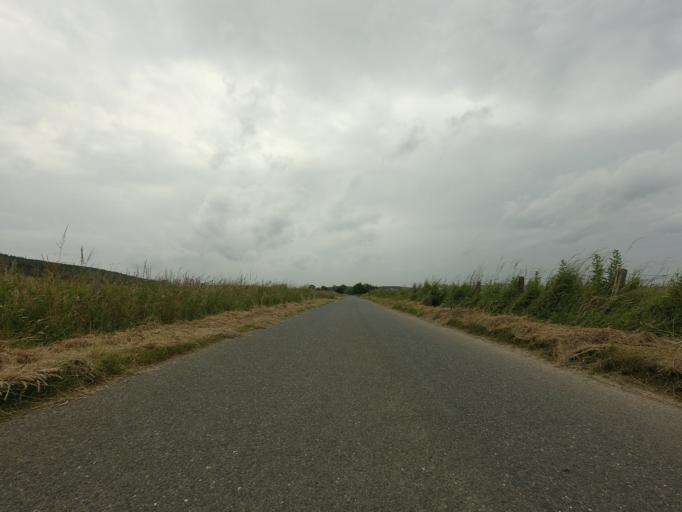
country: GB
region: Scotland
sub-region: Aberdeenshire
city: Portsoy
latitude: 57.6633
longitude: -2.7355
